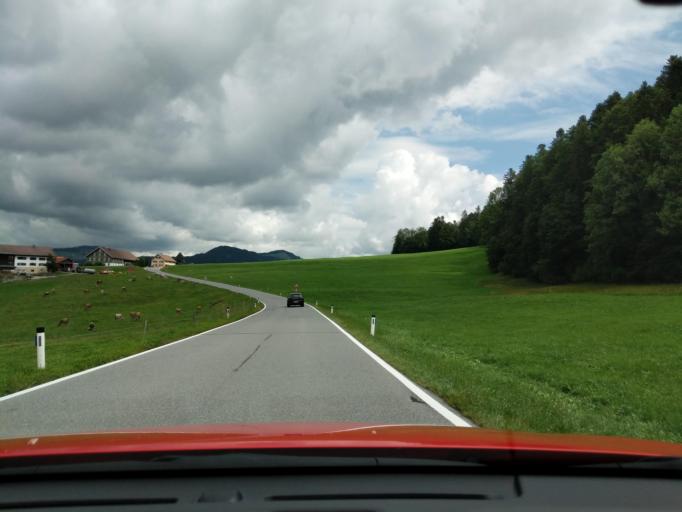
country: AT
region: Vorarlberg
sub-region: Politischer Bezirk Bregenz
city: Riefensberg
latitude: 47.5085
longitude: 9.9503
